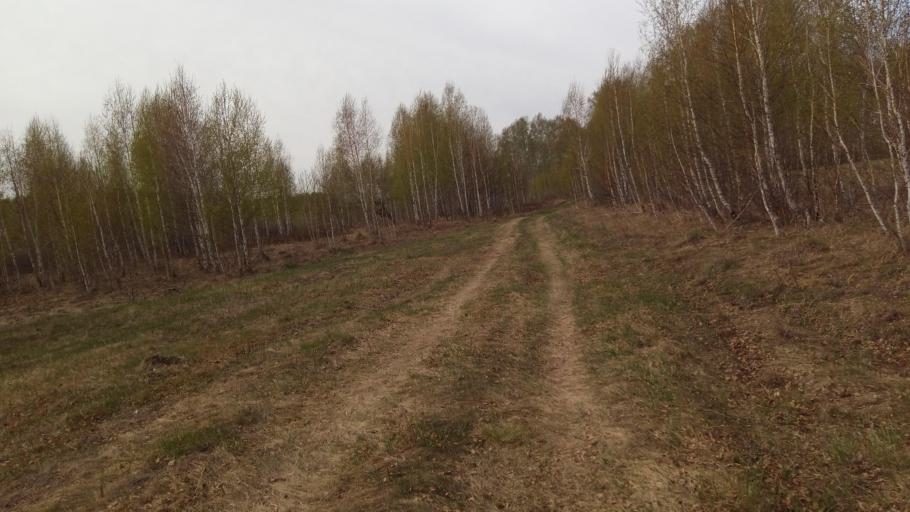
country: RU
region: Chelyabinsk
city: Timiryazevskiy
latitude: 55.0072
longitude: 60.8584
